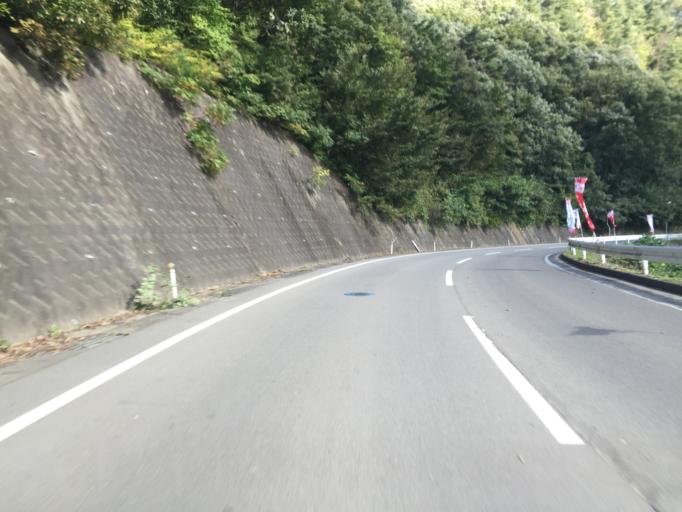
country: JP
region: Fukushima
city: Yanagawamachi-saiwaicho
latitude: 37.8553
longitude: 140.6450
